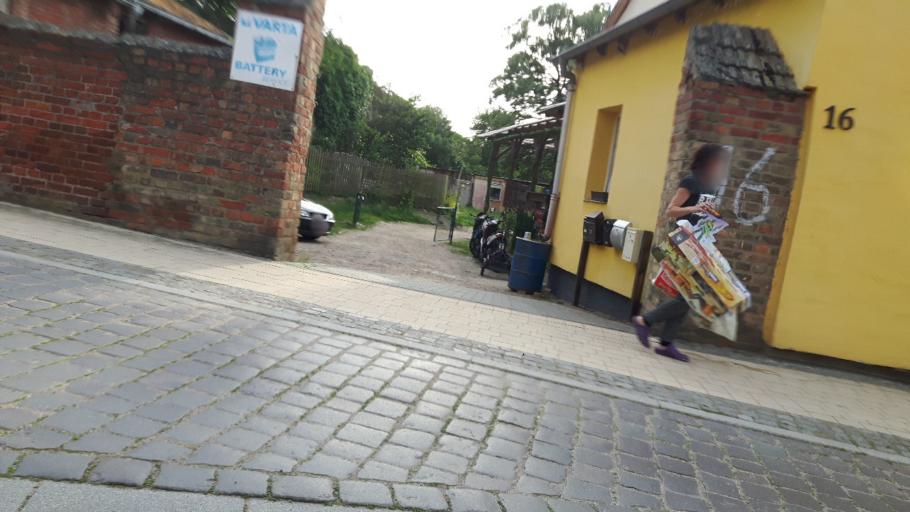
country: DE
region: Brandenburg
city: Gartz
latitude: 53.2097
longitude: 14.3937
